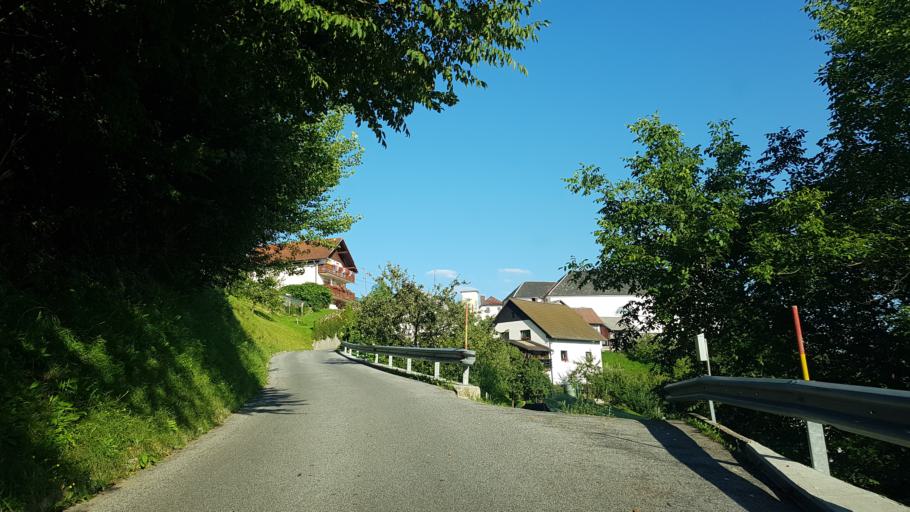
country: SI
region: Cerkno
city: Cerkno
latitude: 46.0803
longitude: 13.9900
